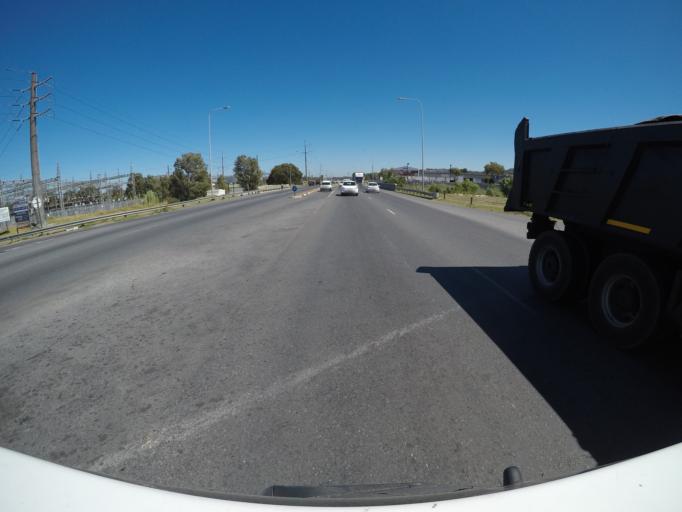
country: ZA
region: Western Cape
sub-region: Cape Winelands District Municipality
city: Stellenbosch
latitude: -34.0913
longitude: 18.8416
